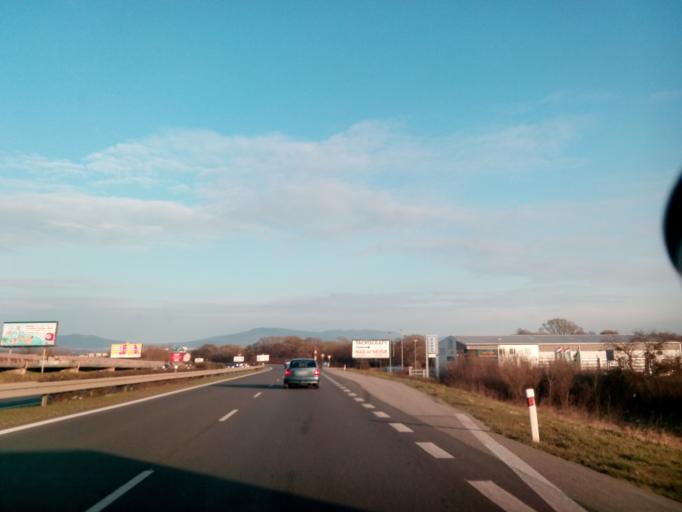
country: SK
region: Kosicky
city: Kosice
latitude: 48.6898
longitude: 21.2456
